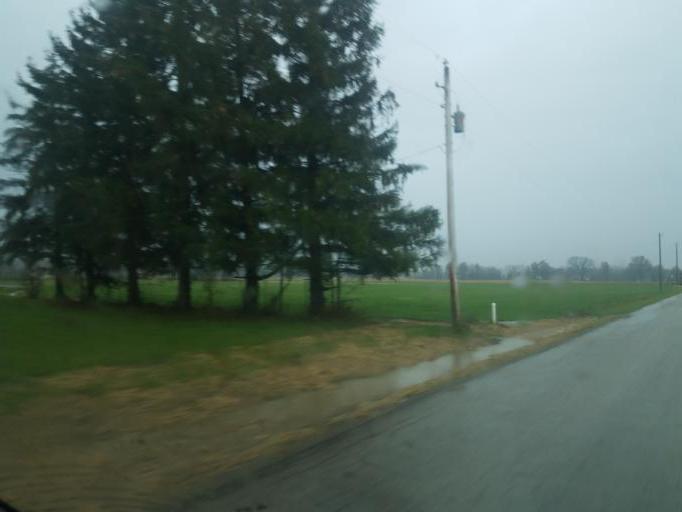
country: US
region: Ohio
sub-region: Morrow County
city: Cardington
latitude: 40.4518
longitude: -82.8716
